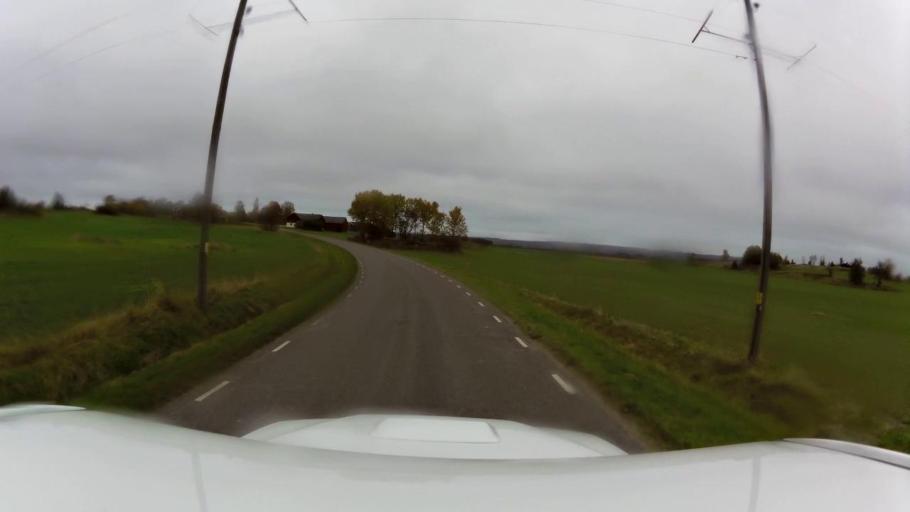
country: SE
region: OEstergoetland
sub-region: Linkopings Kommun
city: Linghem
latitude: 58.4801
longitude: 15.7567
